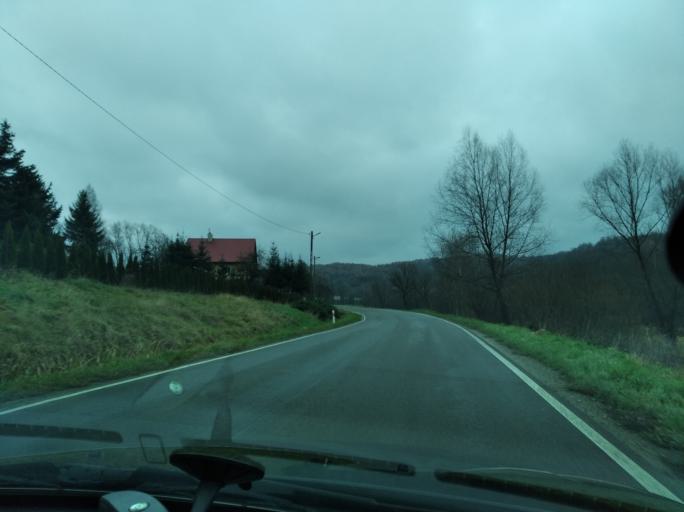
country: PL
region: Subcarpathian Voivodeship
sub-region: Powiat przeworski
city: Manasterz
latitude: 49.9211
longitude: 22.3131
